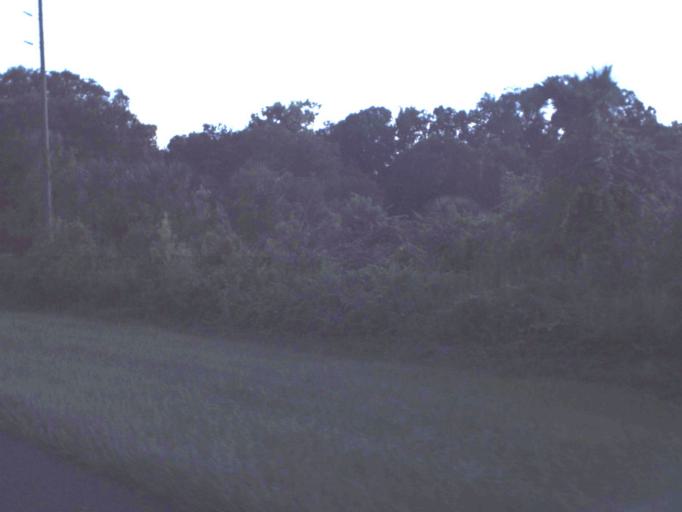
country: US
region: Florida
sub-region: Levy County
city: Inglis
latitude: 28.9674
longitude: -82.6343
